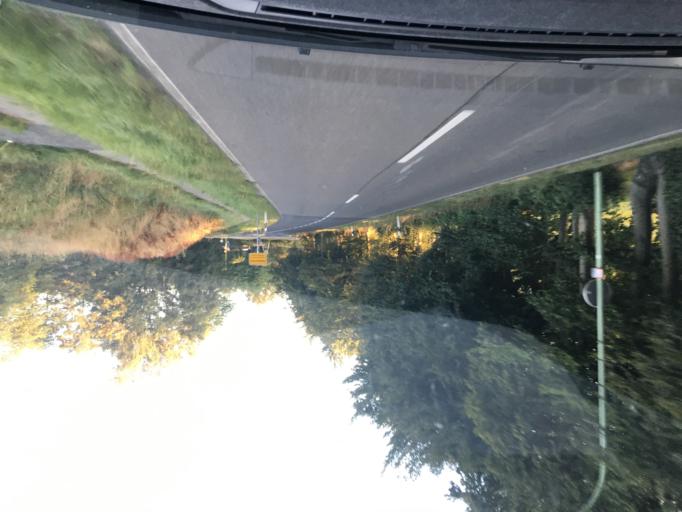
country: DE
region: North Rhine-Westphalia
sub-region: Regierungsbezirk Koln
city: Simmerath
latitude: 50.6353
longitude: 6.3201
